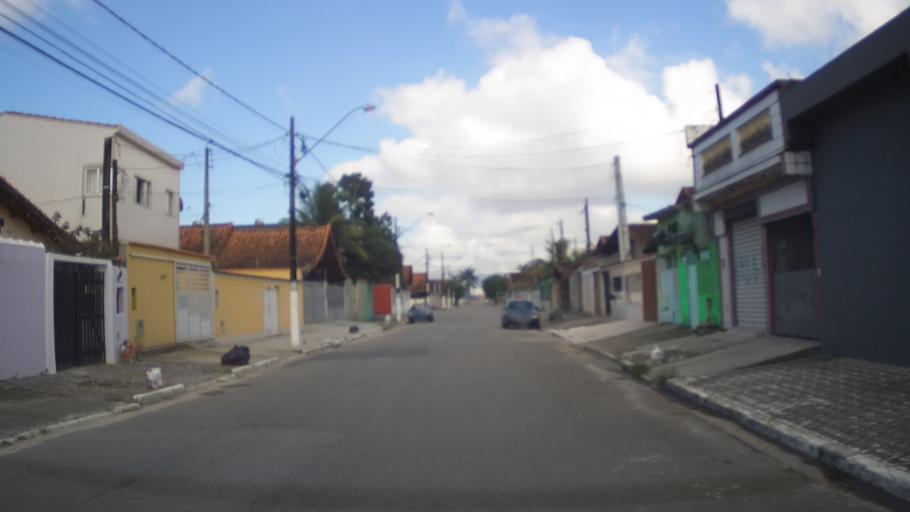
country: BR
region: Sao Paulo
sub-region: Praia Grande
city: Praia Grande
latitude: -24.0173
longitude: -46.4711
